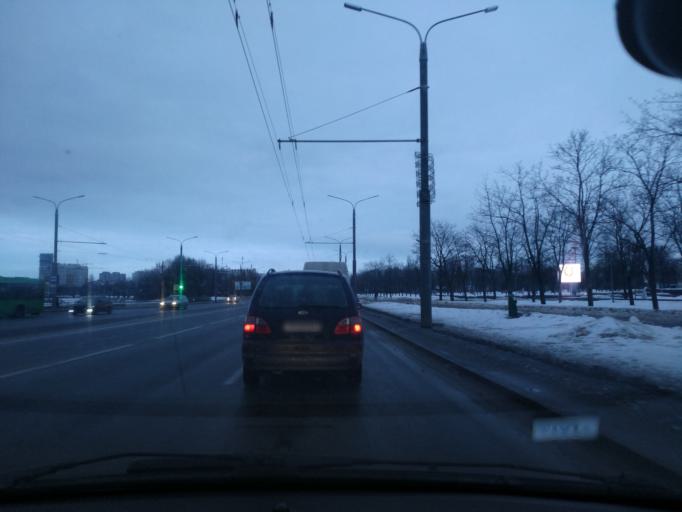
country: BY
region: Mogilev
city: Mahilyow
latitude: 53.8875
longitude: 30.3310
